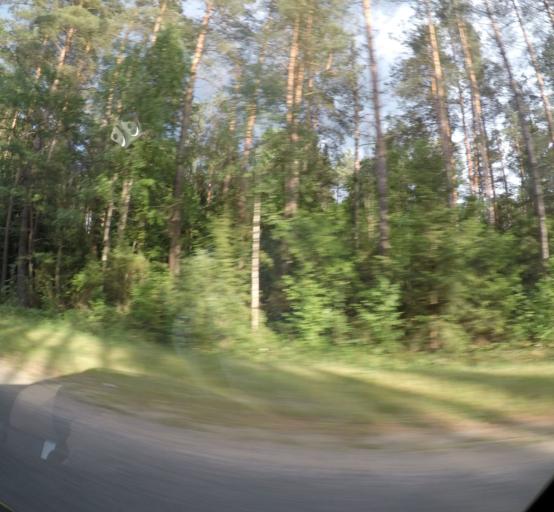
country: LT
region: Alytaus apskritis
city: Druskininkai
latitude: 53.8182
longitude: 24.0453
